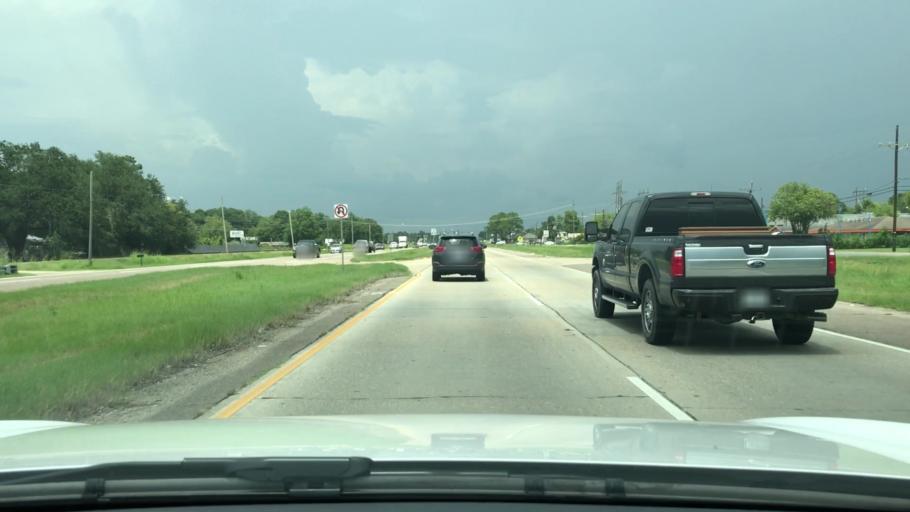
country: US
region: Louisiana
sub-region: West Baton Rouge Parish
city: Brusly
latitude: 30.3778
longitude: -91.2514
